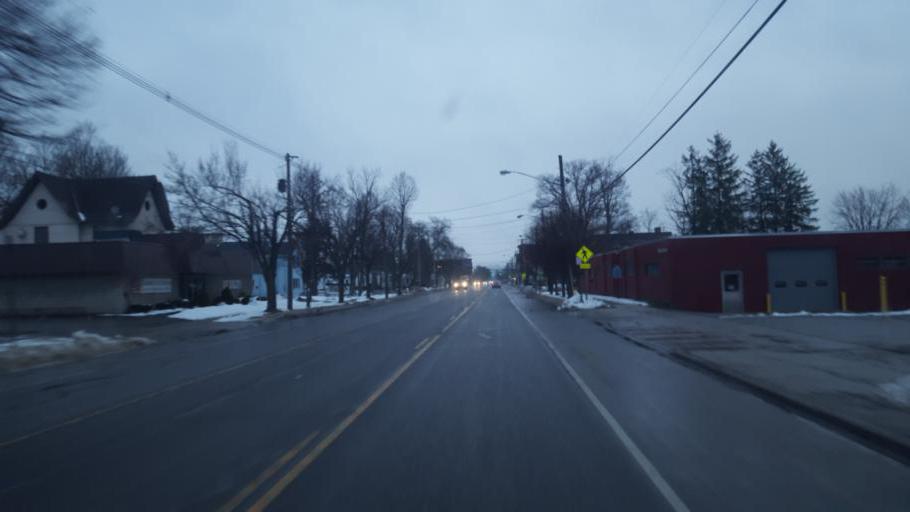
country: US
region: New York
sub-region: Chautauqua County
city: Falconer
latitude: 42.1165
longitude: -79.2007
